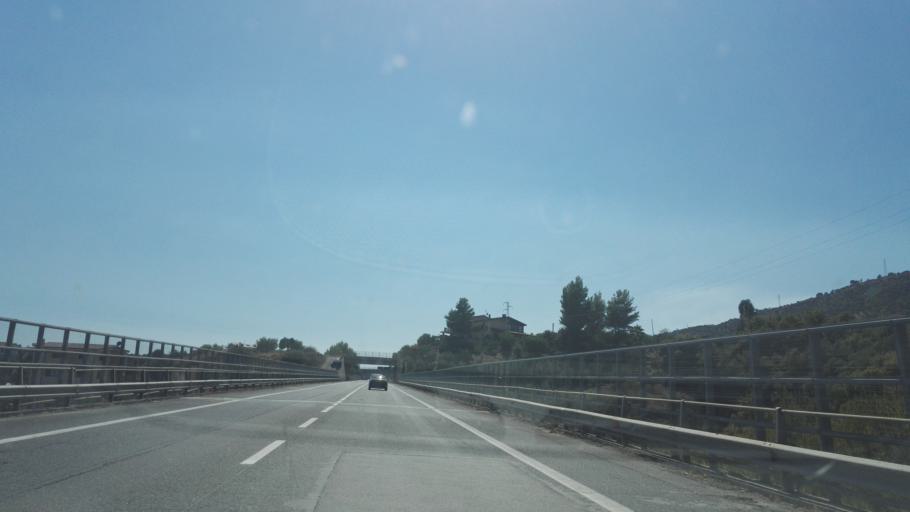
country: IT
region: Calabria
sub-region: Provincia di Cosenza
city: Trebisacce
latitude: 39.8765
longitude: 16.5336
